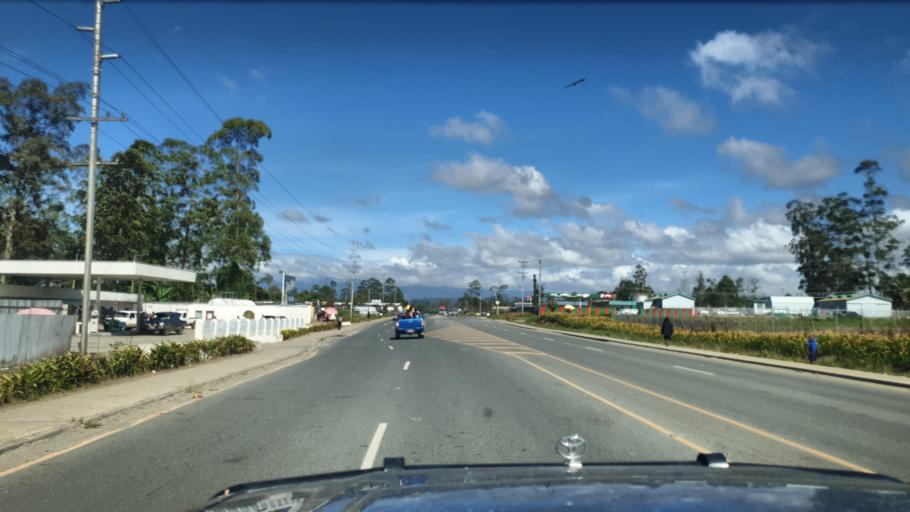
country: PG
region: Western Highlands
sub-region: Hagen
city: Mount Hagen
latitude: -5.8419
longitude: 144.2819
